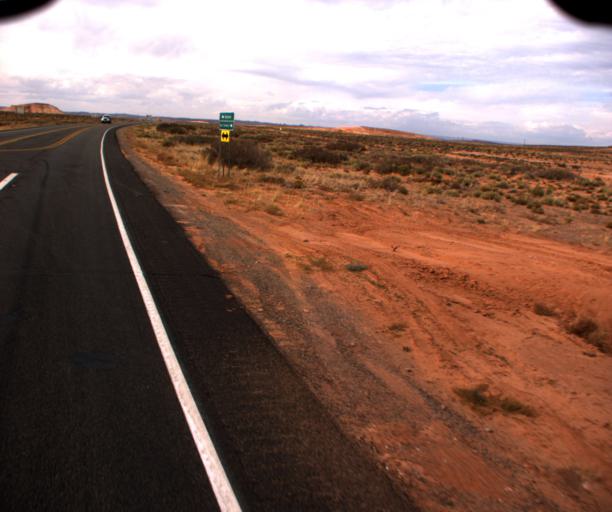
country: US
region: Arizona
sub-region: Apache County
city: Many Farms
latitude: 36.9252
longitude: -109.6146
